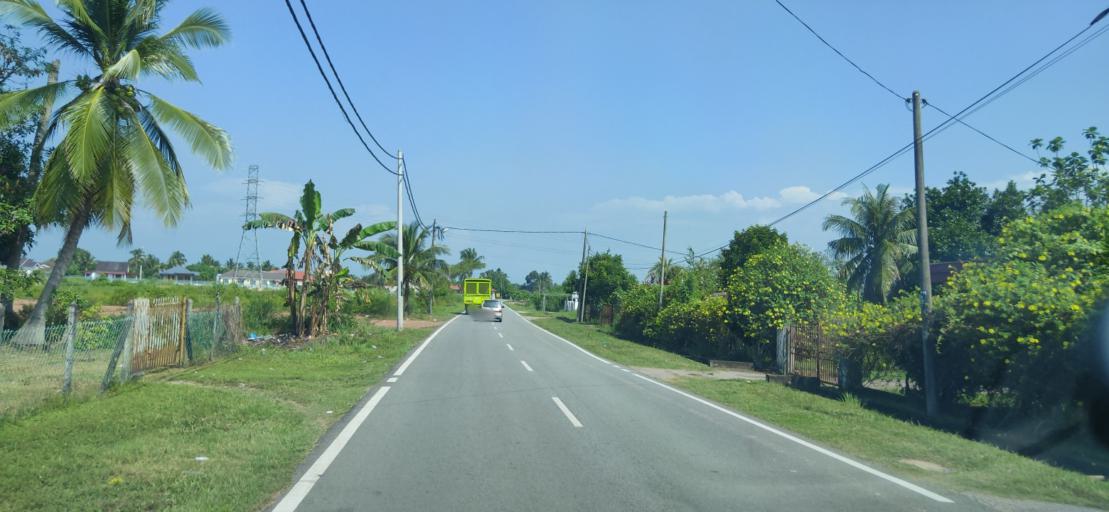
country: MY
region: Kedah
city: Sungai Petani
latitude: 5.6589
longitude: 100.4736
